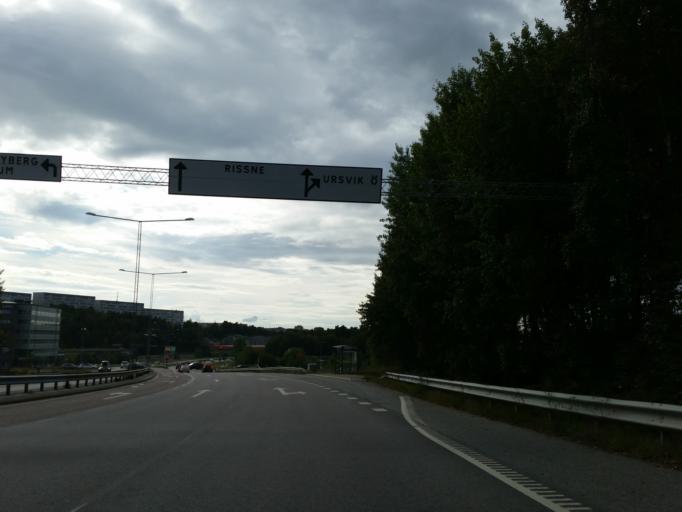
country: SE
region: Stockholm
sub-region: Solna Kommun
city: Rasunda
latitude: 59.3813
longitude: 17.9729
